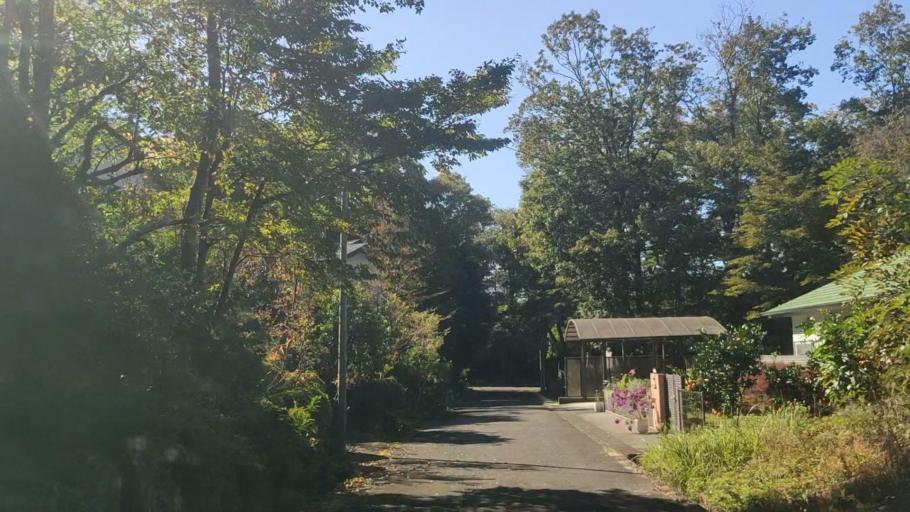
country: JP
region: Shizuoka
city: Ito
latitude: 34.9449
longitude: 139.0121
